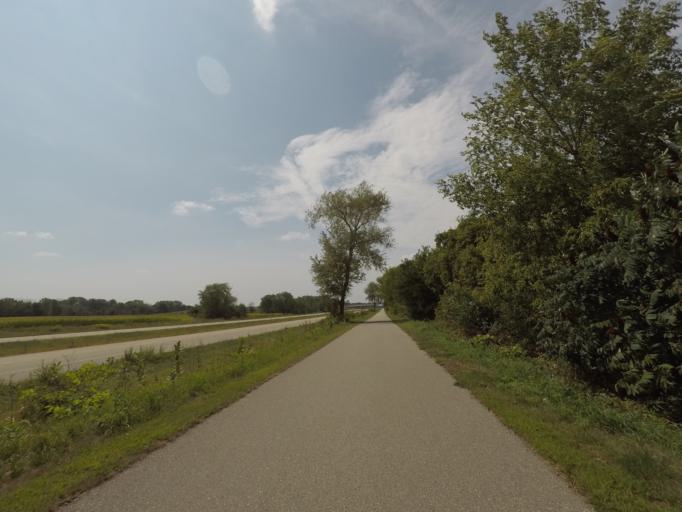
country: US
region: Wisconsin
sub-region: Jefferson County
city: Lake Koshkonong
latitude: 42.8719
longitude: -88.8906
